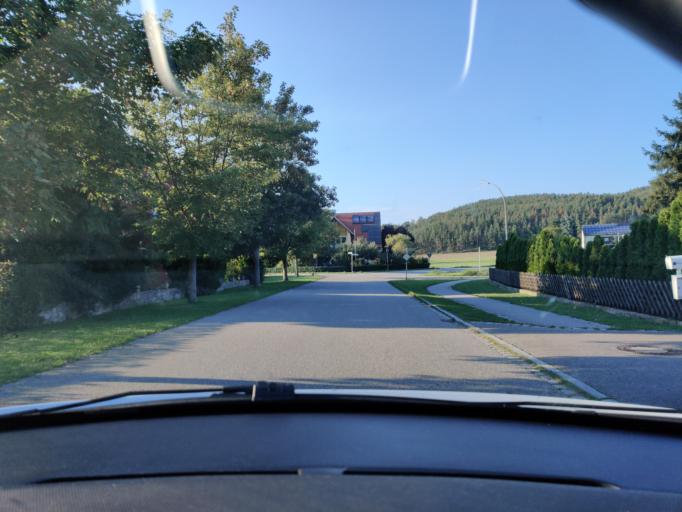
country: DE
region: Bavaria
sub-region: Upper Palatinate
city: Stulln
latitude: 49.4113
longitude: 12.1674
